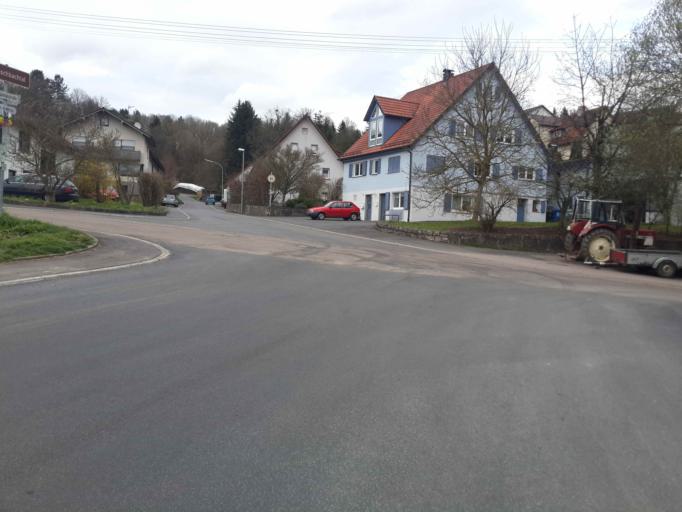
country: DE
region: Baden-Wuerttemberg
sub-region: Karlsruhe Region
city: Adelsheim
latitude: 49.3814
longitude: 9.3798
